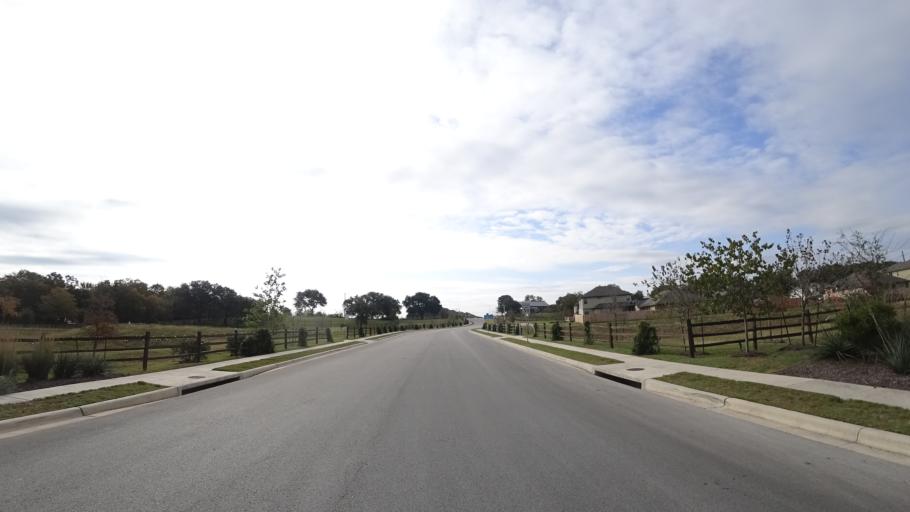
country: US
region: Texas
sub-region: Travis County
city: Manchaca
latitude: 30.1381
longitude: -97.8479
